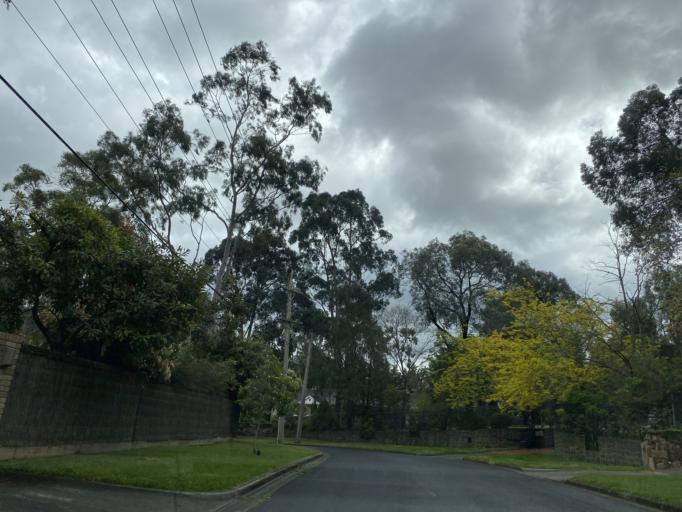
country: AU
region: Victoria
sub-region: Manningham
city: Templestowe Lower
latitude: -37.7655
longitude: 145.1364
